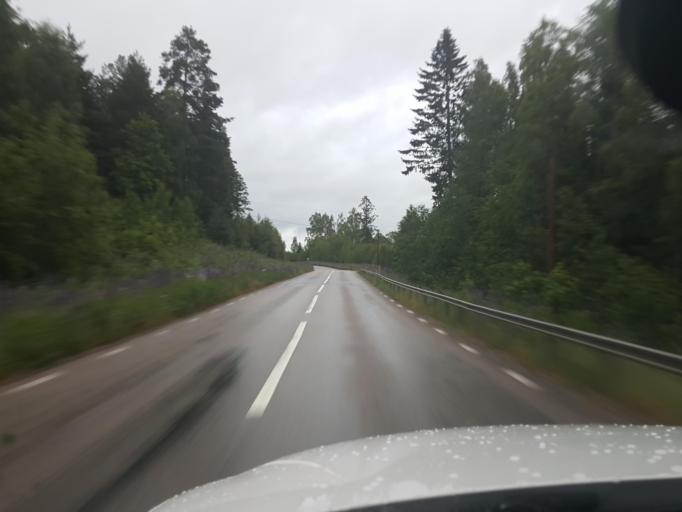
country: SE
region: Gaevleborg
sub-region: Bollnas Kommun
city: Kilafors
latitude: 61.2509
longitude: 16.6097
